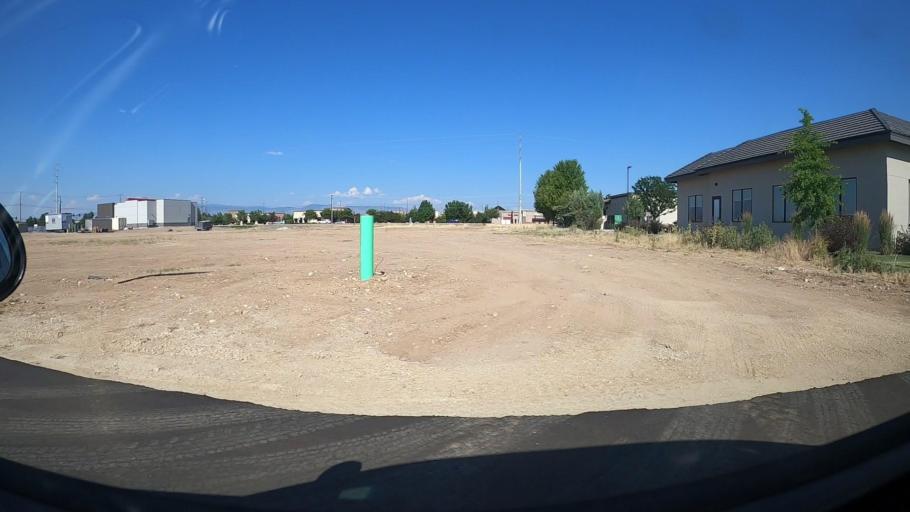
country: US
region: Idaho
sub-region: Ada County
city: Meridian
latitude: 43.6321
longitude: -116.3563
